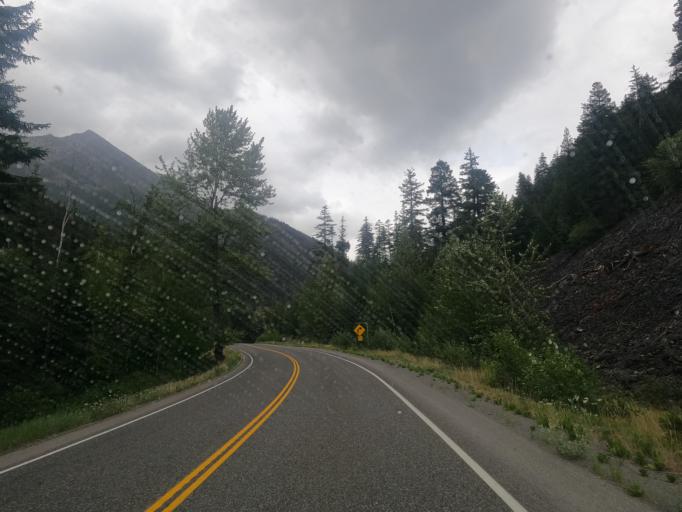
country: CA
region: British Columbia
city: Lillooet
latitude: 50.4860
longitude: -122.2061
